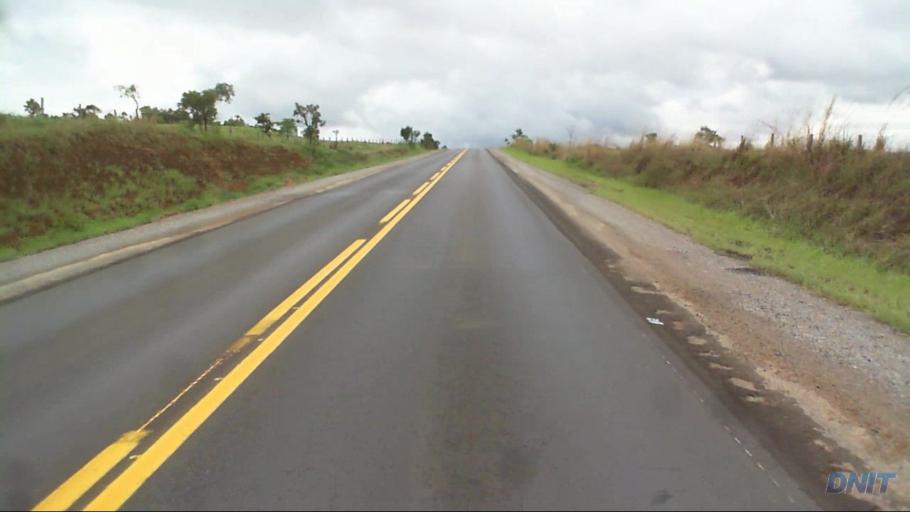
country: BR
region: Goias
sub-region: Padre Bernardo
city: Padre Bernardo
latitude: -15.2186
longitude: -48.5165
